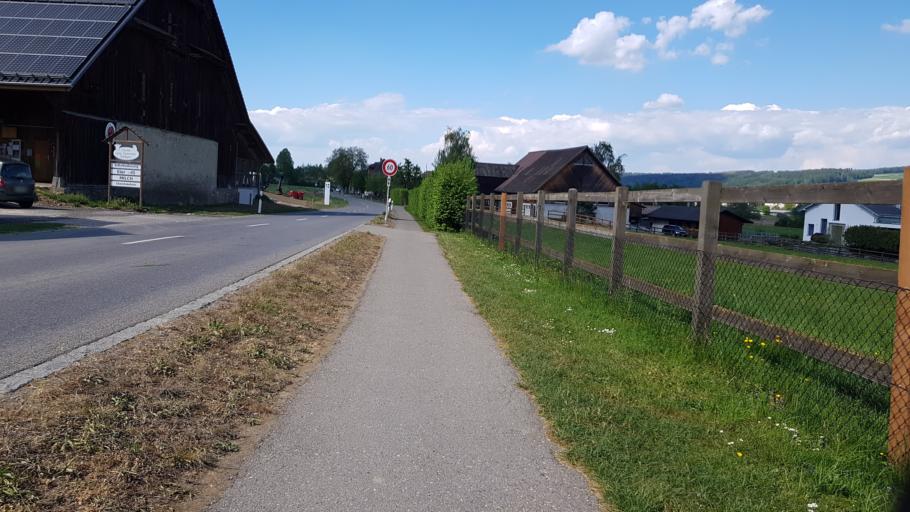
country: CH
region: Lucerne
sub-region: Hochdorf District
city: Hitzkirch
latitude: 47.2102
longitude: 8.2426
